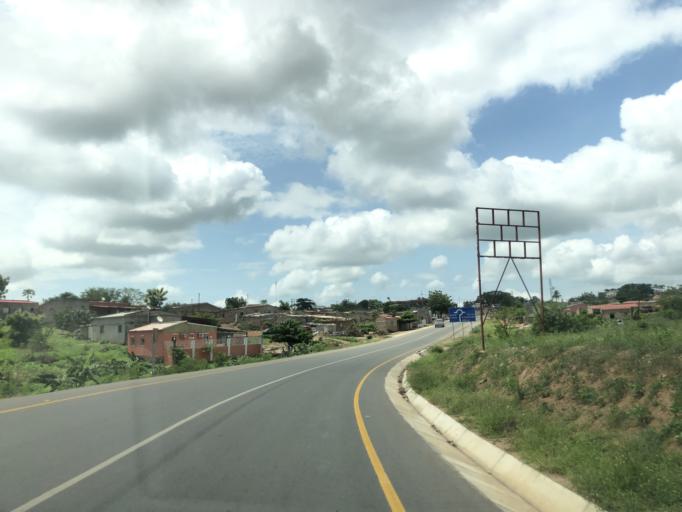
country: AO
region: Cuanza Norte
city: N'dalatando
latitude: -9.6824
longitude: 14.4744
